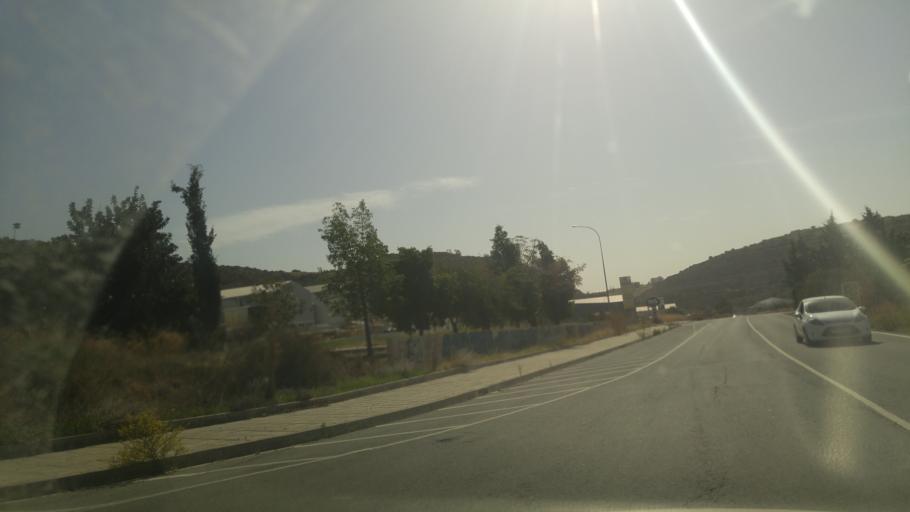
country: CY
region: Limassol
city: Pano Polemidia
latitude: 34.7251
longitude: 33.0296
